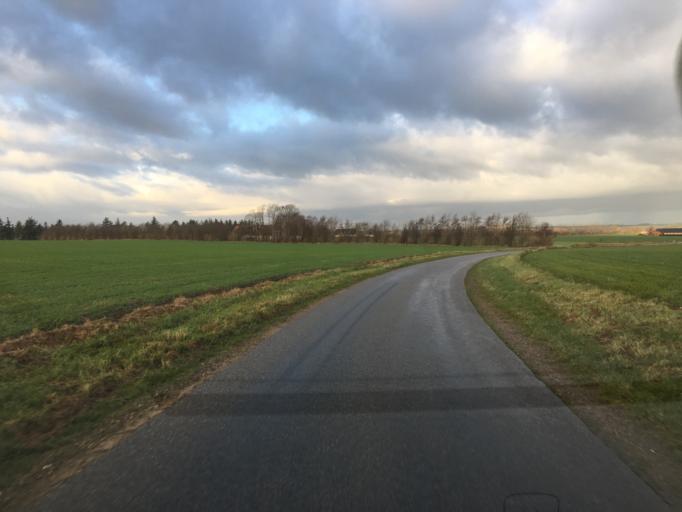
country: DK
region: South Denmark
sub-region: Tonder Kommune
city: Sherrebek
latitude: 55.1640
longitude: 8.8120
